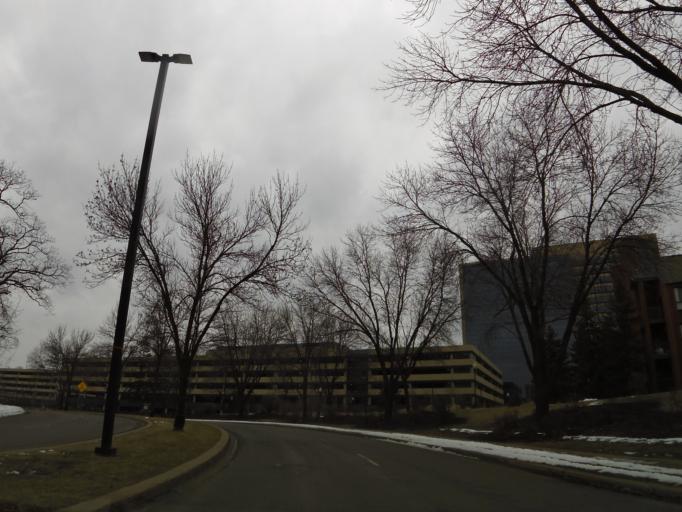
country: US
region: Minnesota
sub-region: Hennepin County
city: Minnetonka Mills
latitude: 44.8881
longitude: -93.4152
